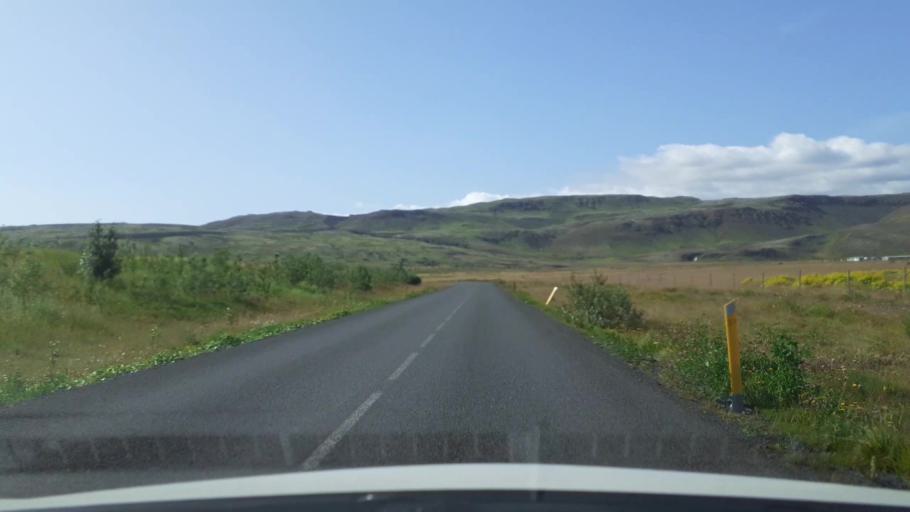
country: IS
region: South
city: Hveragerdi
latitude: 64.0124
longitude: -21.1945
